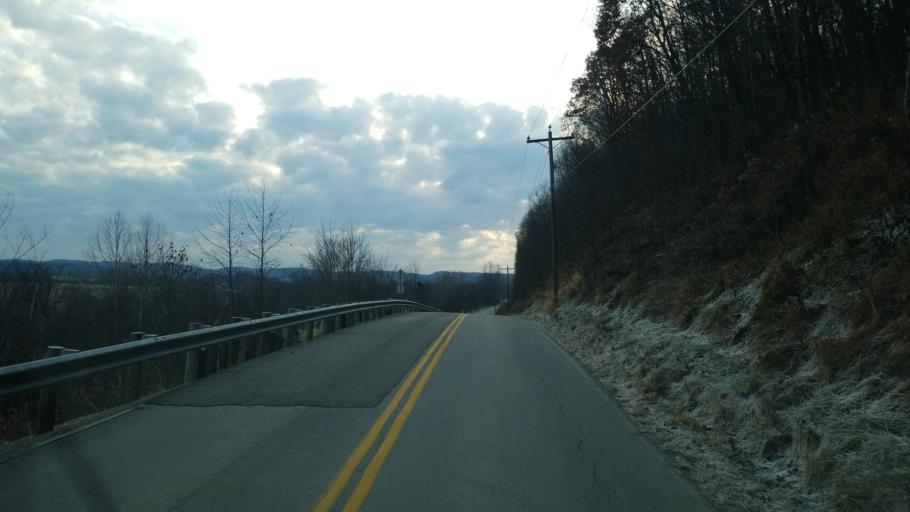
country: US
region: Ohio
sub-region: Pike County
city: Waverly
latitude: 39.2161
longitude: -82.8721
